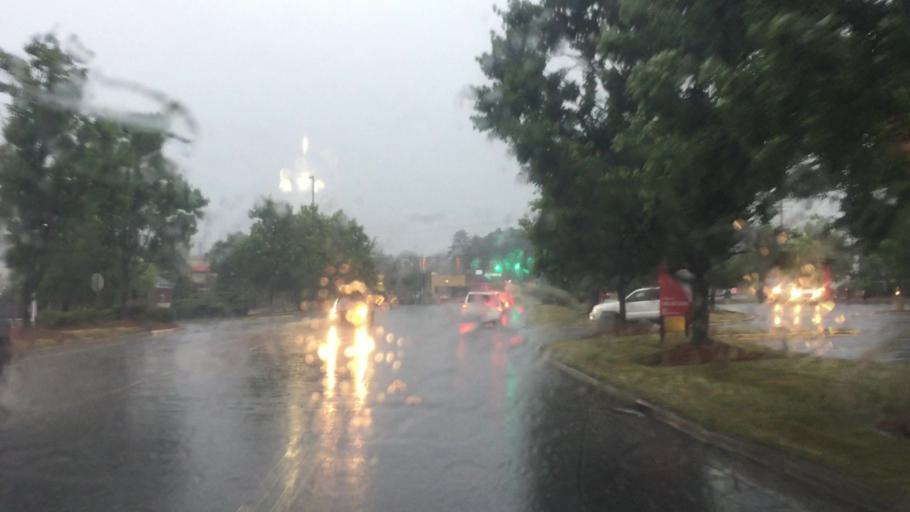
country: US
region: North Carolina
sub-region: Rowan County
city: Salisbury
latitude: 35.6520
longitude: -80.4593
